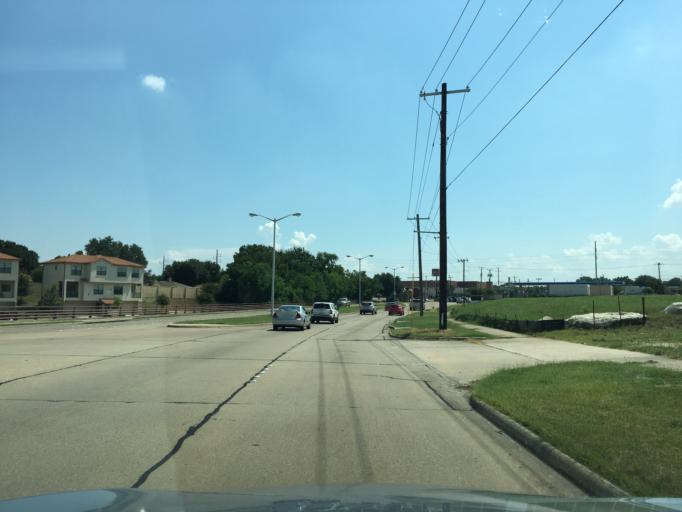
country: US
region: Texas
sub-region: Dallas County
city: Garland
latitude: 32.9474
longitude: -96.6488
